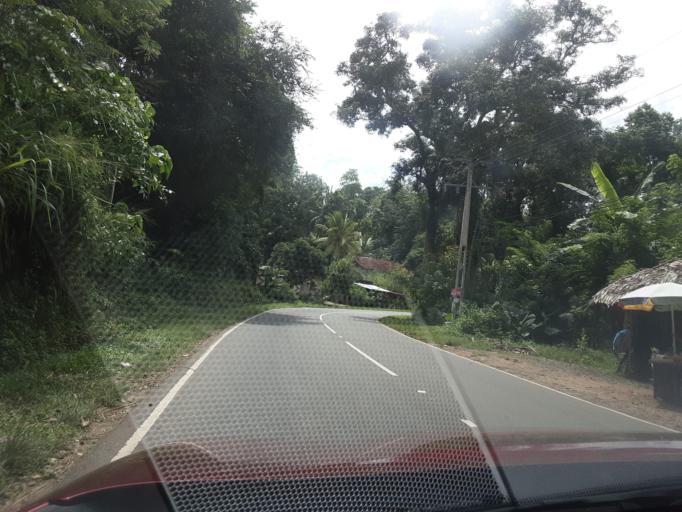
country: LK
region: Uva
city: Monaragala
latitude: 6.8958
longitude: 81.2469
